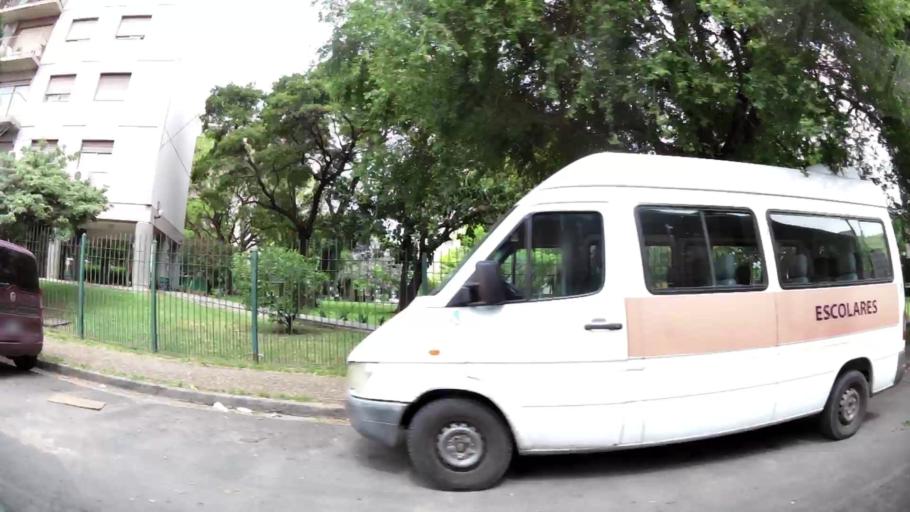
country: AR
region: Buenos Aires F.D.
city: Villa Lugano
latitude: -34.7074
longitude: -58.5038
